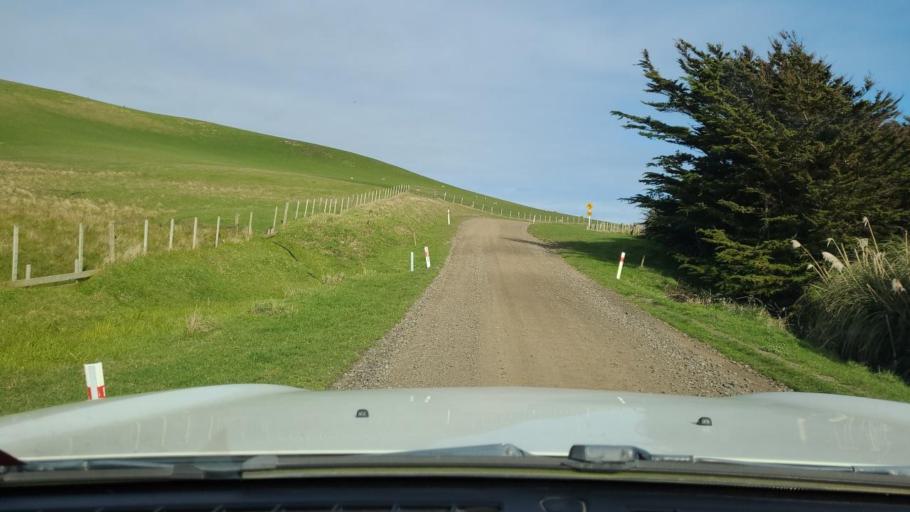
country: NZ
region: Chatham Islands
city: Waitangi
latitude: -44.0185
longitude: -176.6671
